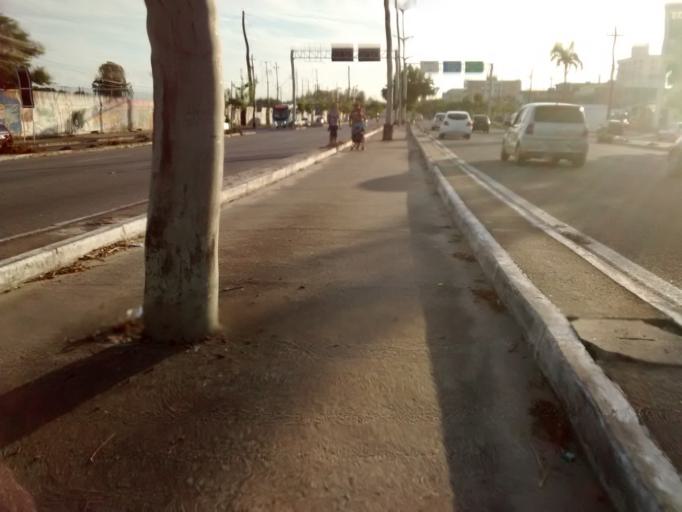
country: BR
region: Ceara
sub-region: Fortaleza
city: Fortaleza
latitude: -3.7371
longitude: -38.5728
